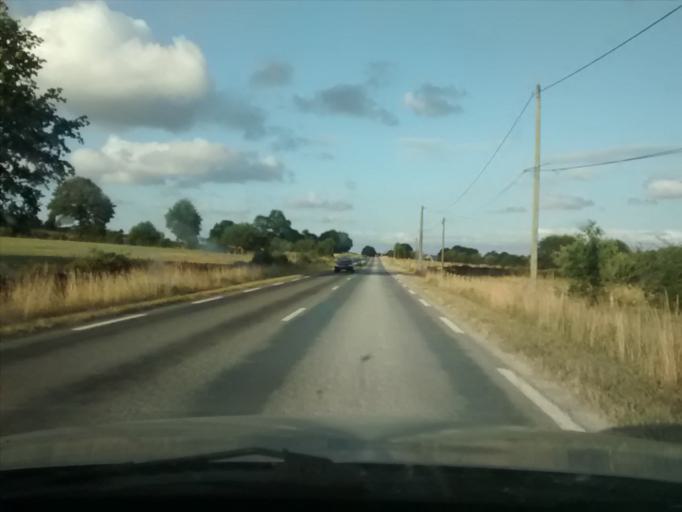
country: FR
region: Pays de la Loire
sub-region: Departement de la Sarthe
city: Sille-le-Guillaume
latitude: 48.1545
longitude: -0.2255
